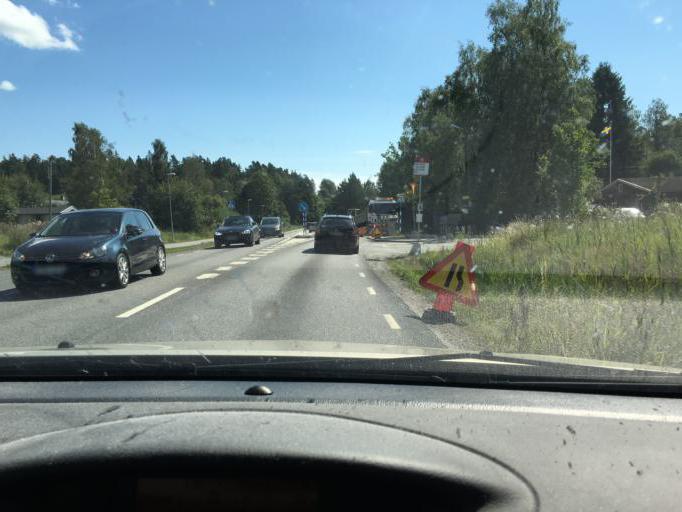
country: SE
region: Stockholm
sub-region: Varmdo Kommun
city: Mortnas
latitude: 59.2847
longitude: 18.4200
